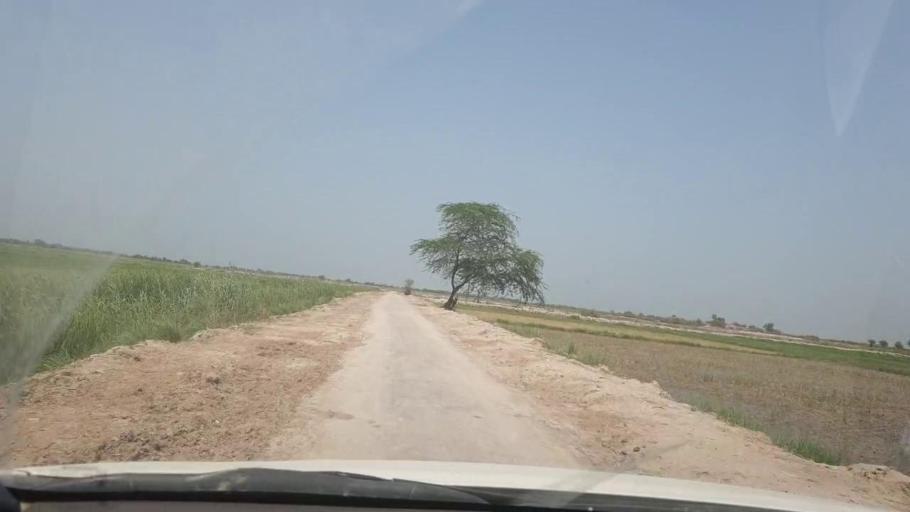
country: PK
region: Sindh
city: Lakhi
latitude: 27.8819
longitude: 68.7368
